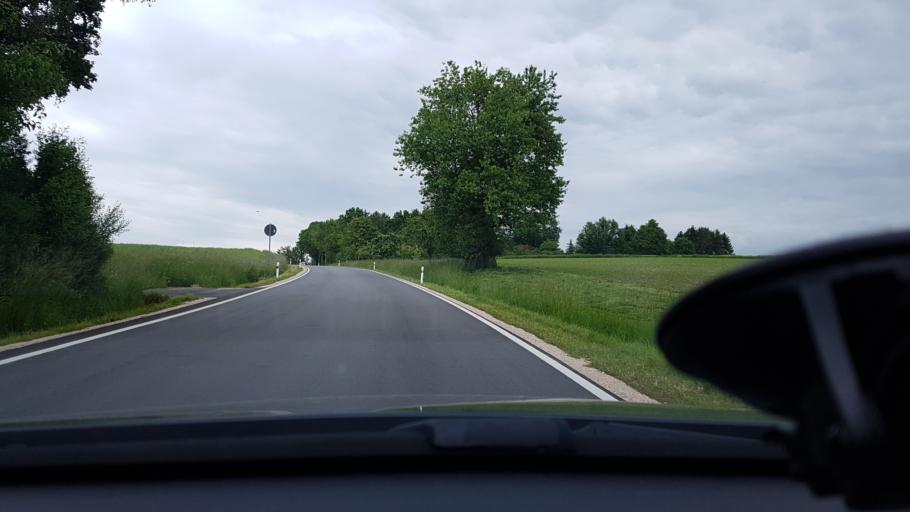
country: DE
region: Bavaria
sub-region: Lower Bavaria
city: Triftern
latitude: 48.3883
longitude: 13.0048
